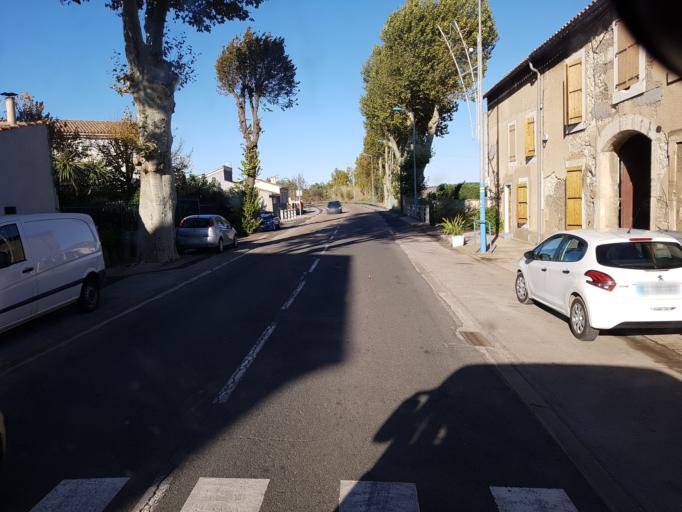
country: FR
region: Languedoc-Roussillon
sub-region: Departement de l'Aude
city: Coursan
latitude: 43.2377
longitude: 3.0585
